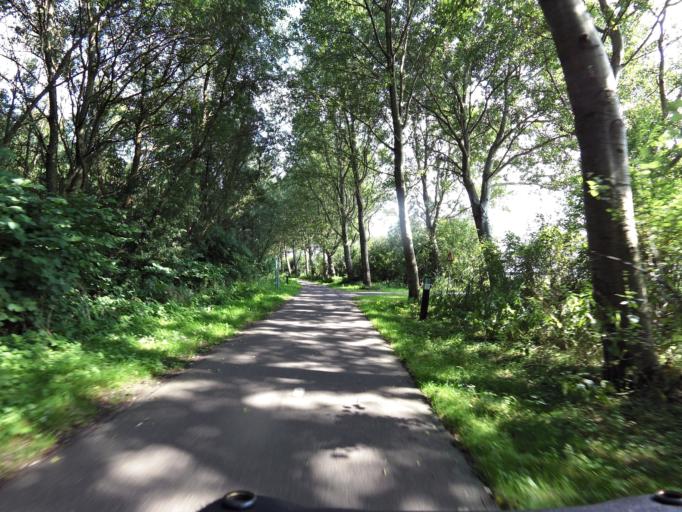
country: NL
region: South Holland
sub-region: Gemeente Binnenmaas
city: Heinenoord
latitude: 51.8267
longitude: 4.5119
